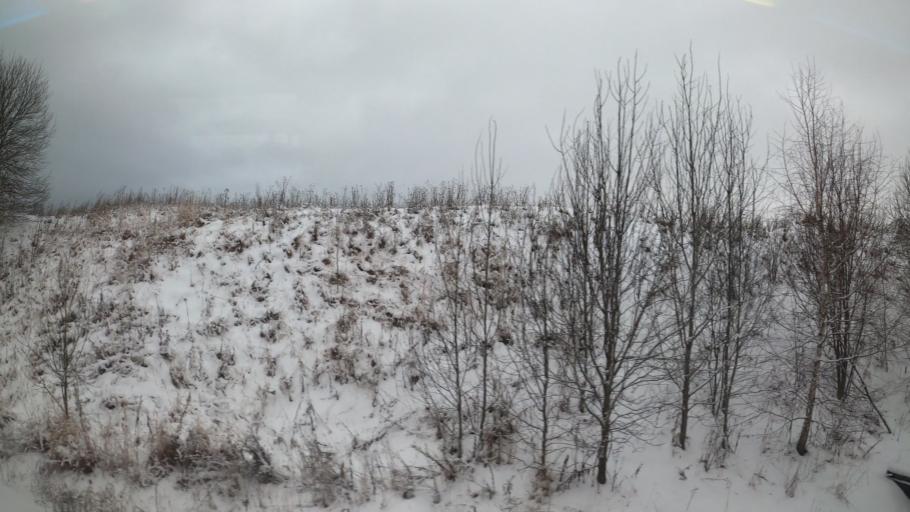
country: RU
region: Jaroslavl
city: Pereslavl'-Zalesskiy
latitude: 56.7032
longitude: 38.9105
